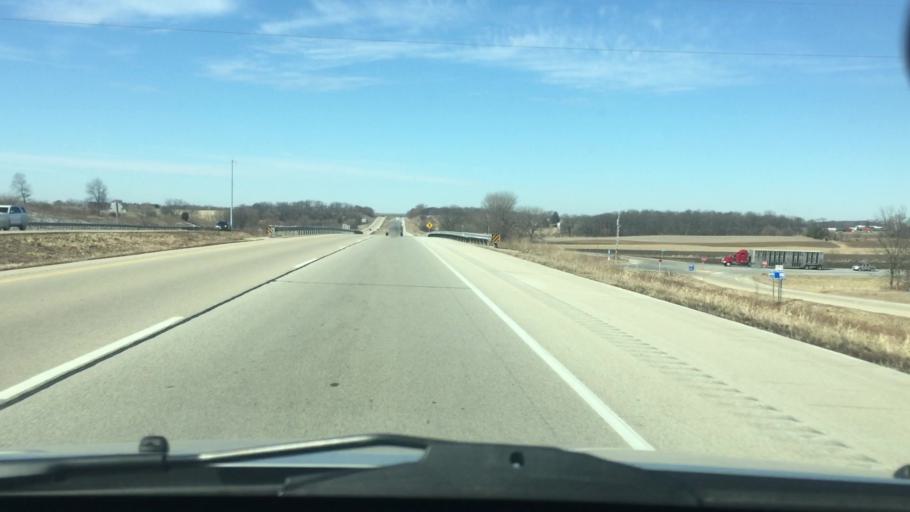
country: US
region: Wisconsin
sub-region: Dane County
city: Deerfield
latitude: 43.1092
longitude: -89.0810
